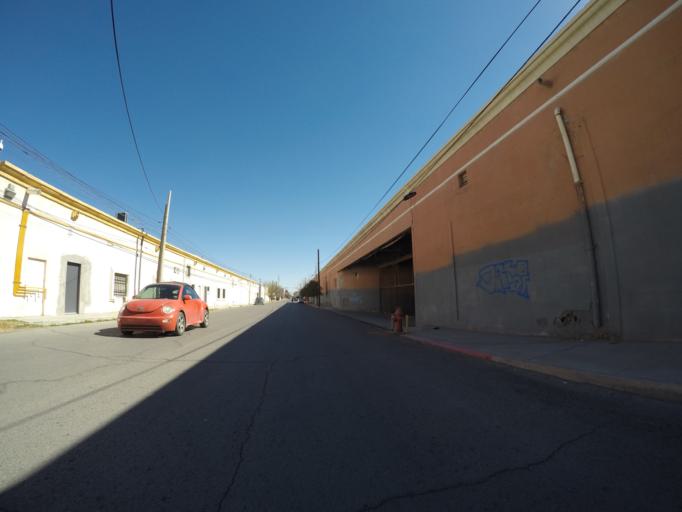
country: MX
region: Chihuahua
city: Ciudad Juarez
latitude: 31.7326
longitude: -106.4490
